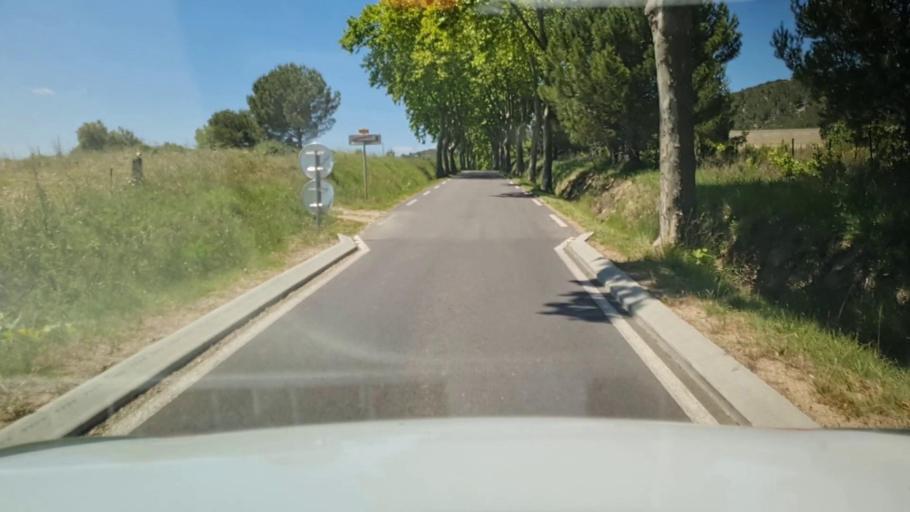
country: FR
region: Languedoc-Roussillon
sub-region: Departement du Gard
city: Clarensac
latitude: 43.8277
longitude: 4.2113
